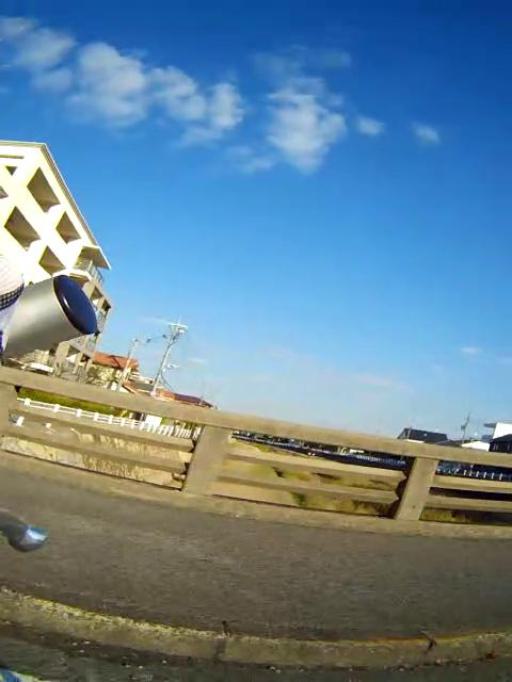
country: JP
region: Hyogo
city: Takarazuka
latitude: 34.7748
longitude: 135.3584
